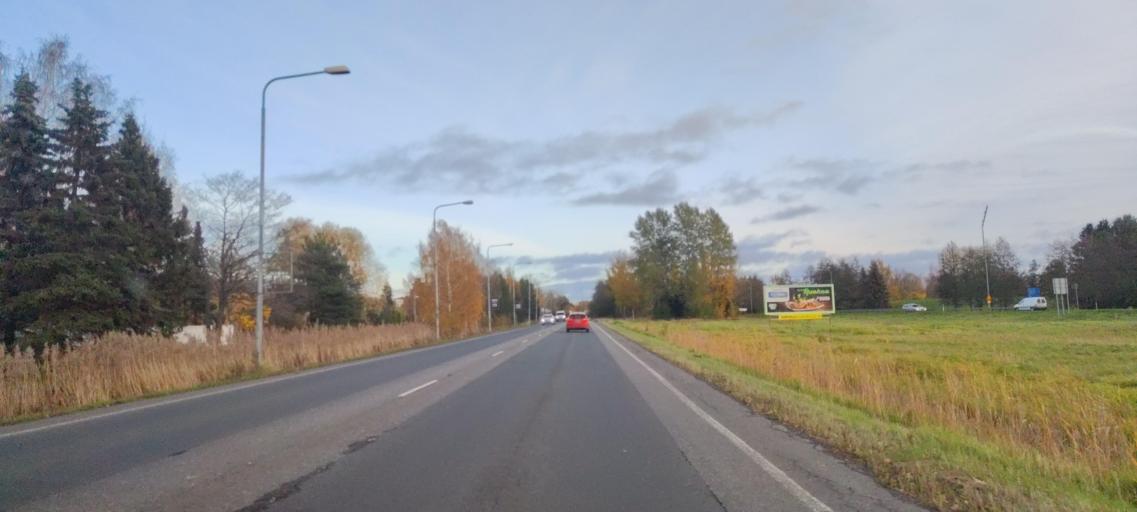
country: FI
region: Satakunta
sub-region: Pori
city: Pori
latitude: 61.4792
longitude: 21.7705
